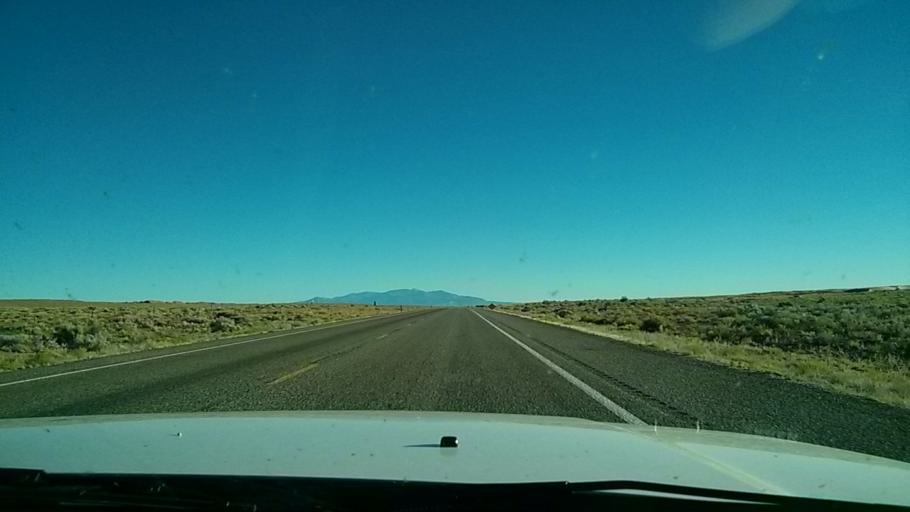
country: US
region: Utah
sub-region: Emery County
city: Ferron
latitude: 38.5930
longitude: -110.5893
